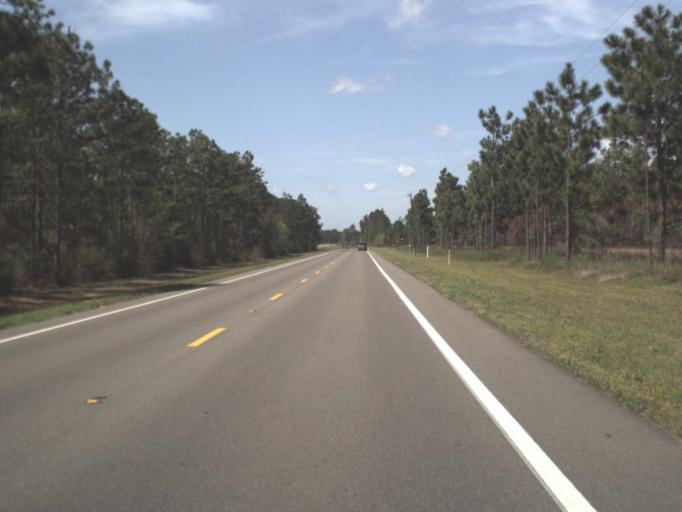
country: US
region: Florida
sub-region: Santa Rosa County
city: East Milton
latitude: 30.6853
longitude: -86.8285
